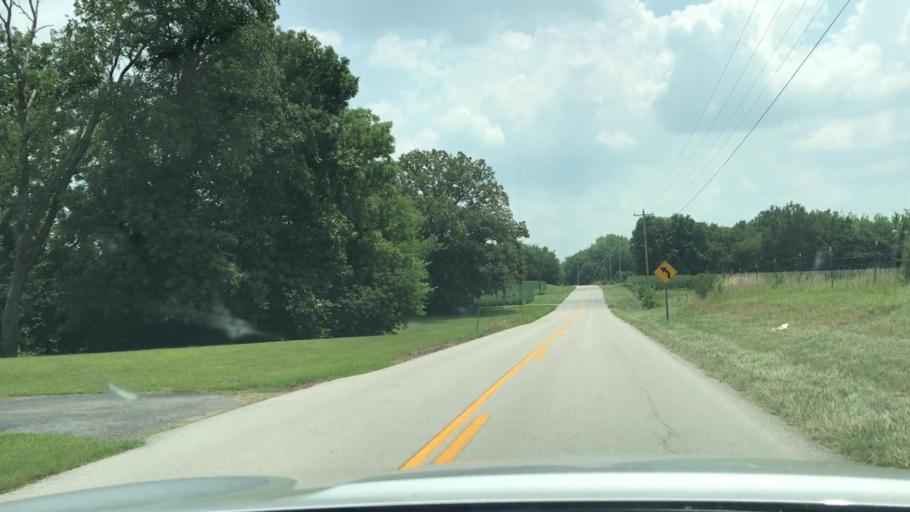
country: US
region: Kentucky
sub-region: Todd County
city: Elkton
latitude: 36.7633
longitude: -87.1066
